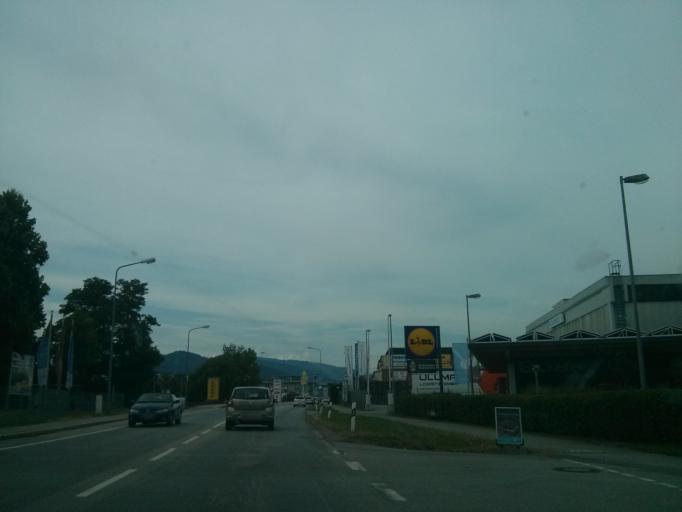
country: DE
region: Bavaria
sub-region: Lower Bavaria
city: Deggendorf
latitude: 48.8478
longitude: 12.9588
